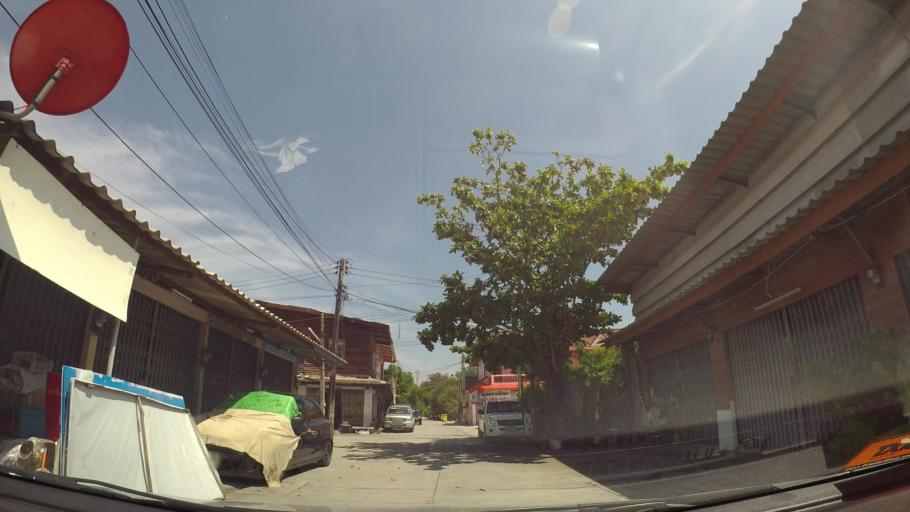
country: TH
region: Chon Buri
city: Chon Buri
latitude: 13.3196
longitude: 100.9568
